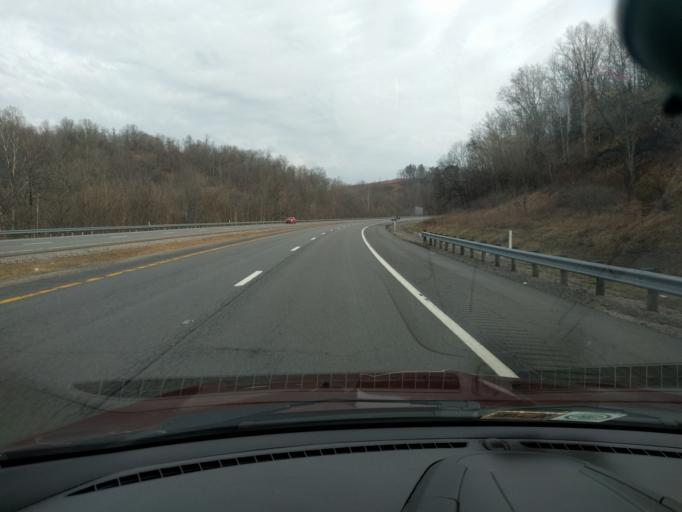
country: US
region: West Virginia
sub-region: Jackson County
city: Ravenswood
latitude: 38.9503
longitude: -81.7041
